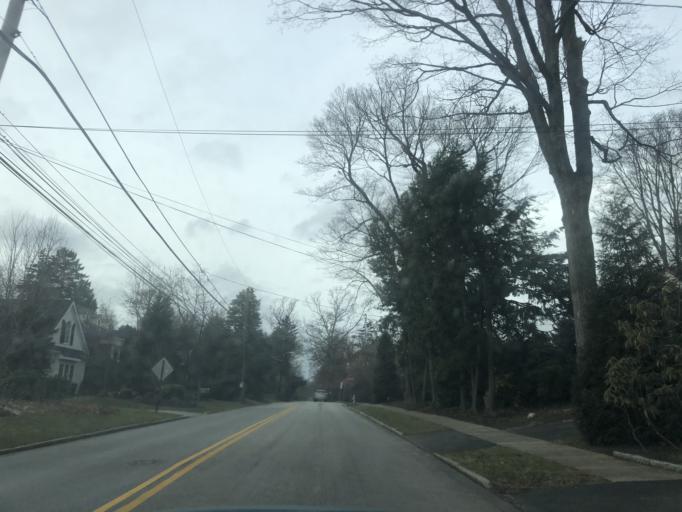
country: US
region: Pennsylvania
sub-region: Montgomery County
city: Bryn Mawr
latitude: 40.0295
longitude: -75.3309
